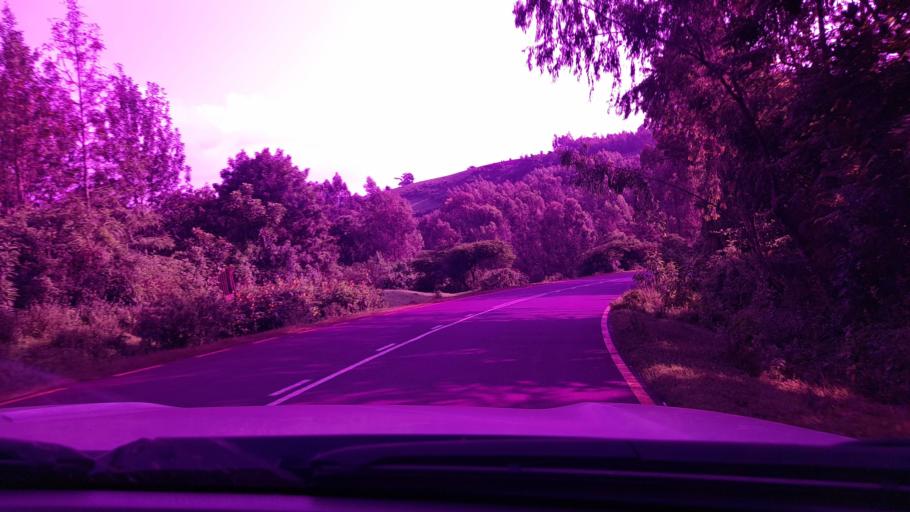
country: ET
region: Oromiya
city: Bedele
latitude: 8.1381
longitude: 36.4512
